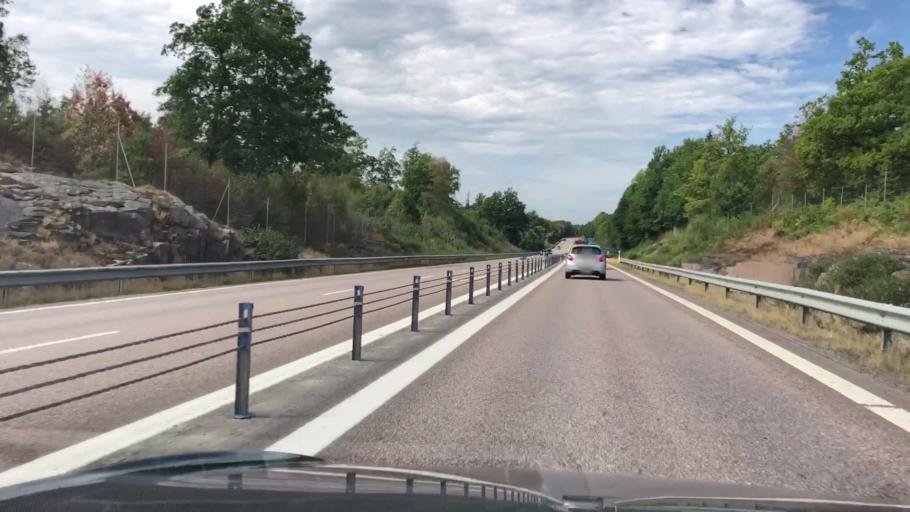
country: SE
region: Blekinge
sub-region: Ronneby Kommun
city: Kallinge
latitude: 56.2041
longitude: 15.3468
